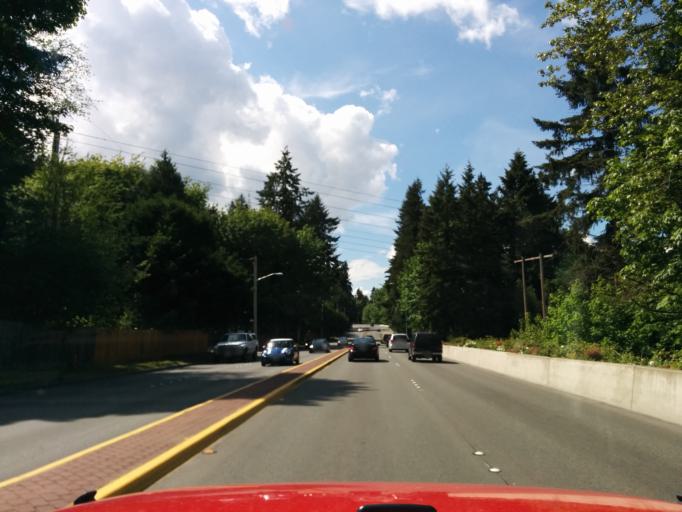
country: US
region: Washington
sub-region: King County
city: Redmond
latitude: 47.6779
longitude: -122.1576
